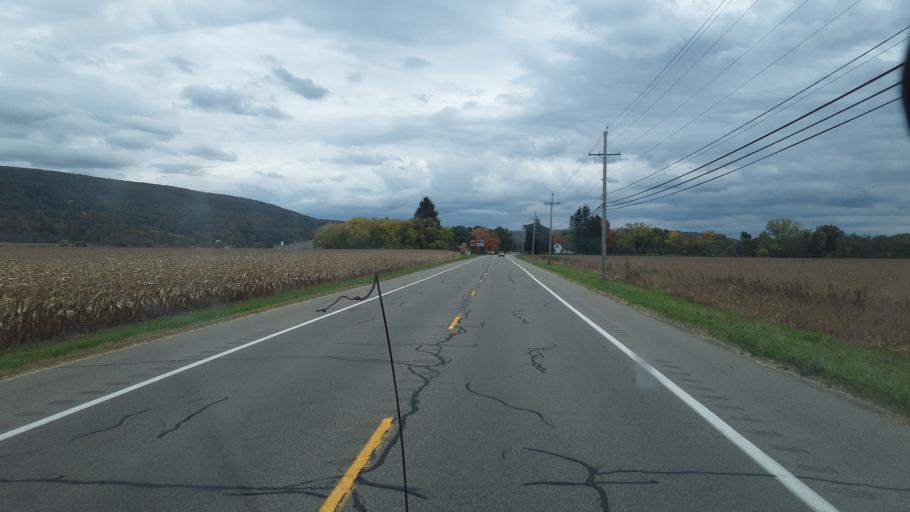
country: US
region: New York
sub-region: Allegany County
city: Belmont
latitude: 42.2056
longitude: -78.0097
